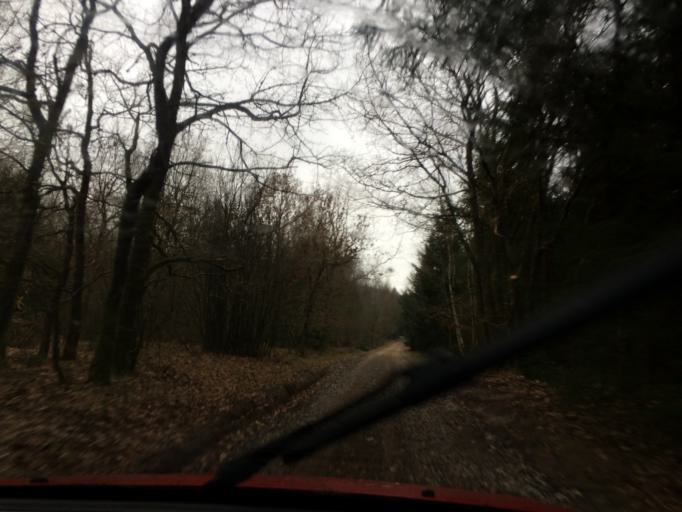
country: DK
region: Central Jutland
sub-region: Silkeborg Kommune
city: Virklund
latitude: 56.0269
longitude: 9.4866
